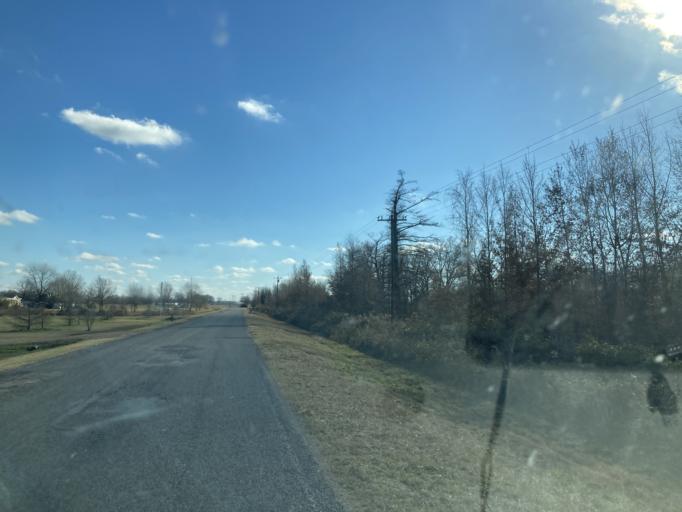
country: US
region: Mississippi
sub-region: Yazoo County
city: Yazoo City
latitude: 32.9345
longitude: -90.4734
